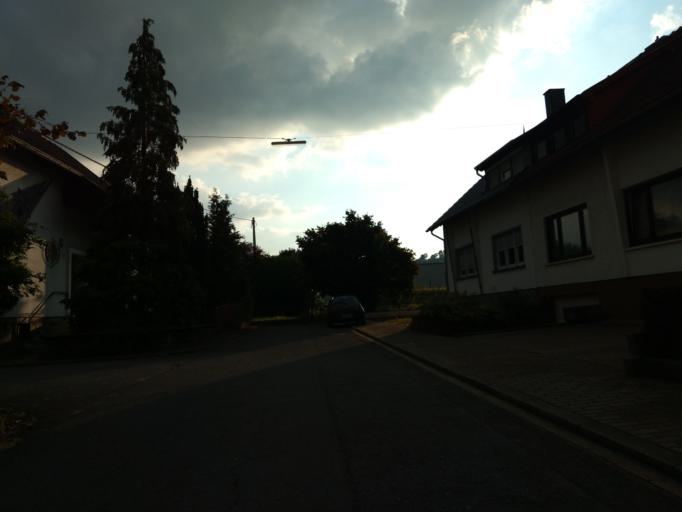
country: DE
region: Saarland
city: Rehlingen-Siersburg
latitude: 49.3737
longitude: 6.6836
